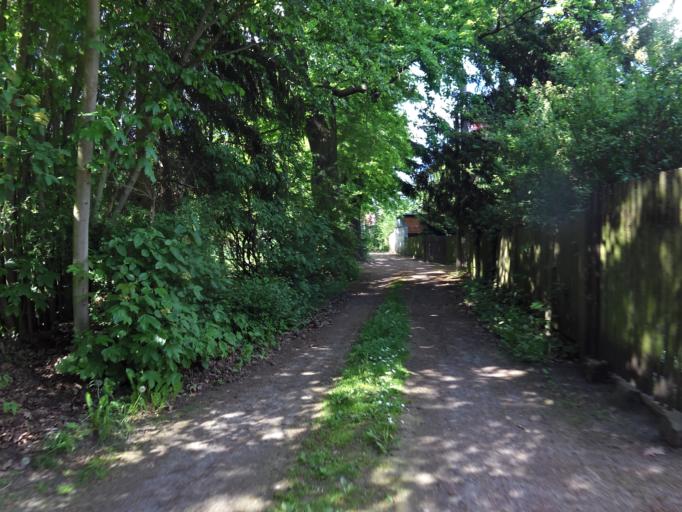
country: DE
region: Saxony
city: Markkleeberg
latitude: 51.2960
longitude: 12.3300
